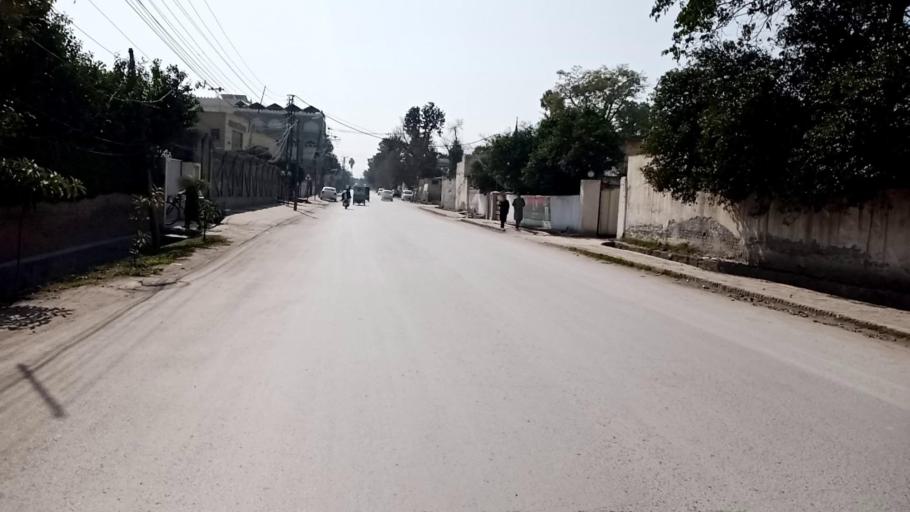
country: PK
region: Khyber Pakhtunkhwa
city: Peshawar
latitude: 33.9967
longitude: 71.5009
